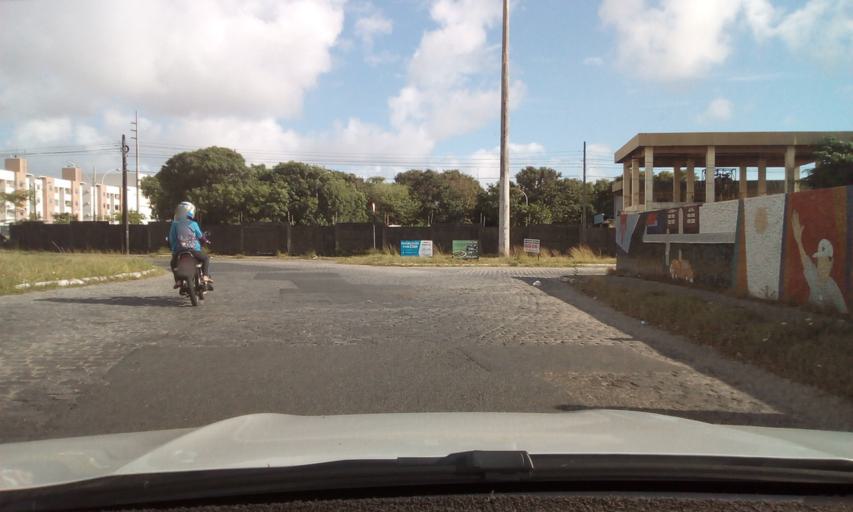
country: BR
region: Paraiba
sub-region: Joao Pessoa
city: Joao Pessoa
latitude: -7.1657
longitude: -34.8281
